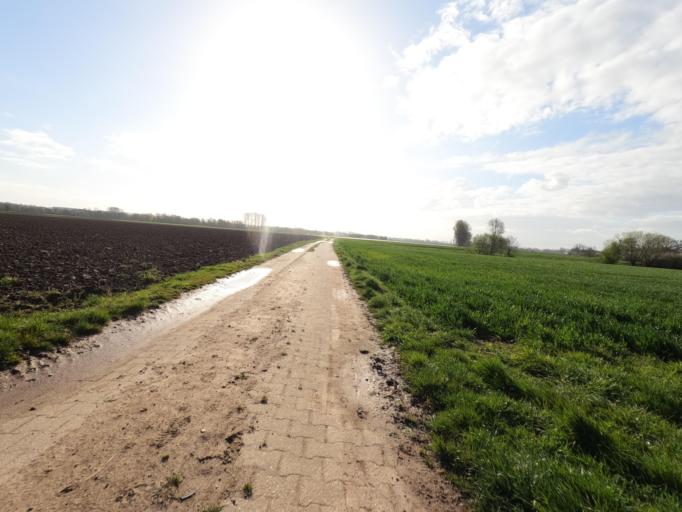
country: DE
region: North Rhine-Westphalia
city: Huckelhoven
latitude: 51.0310
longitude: 6.2223
